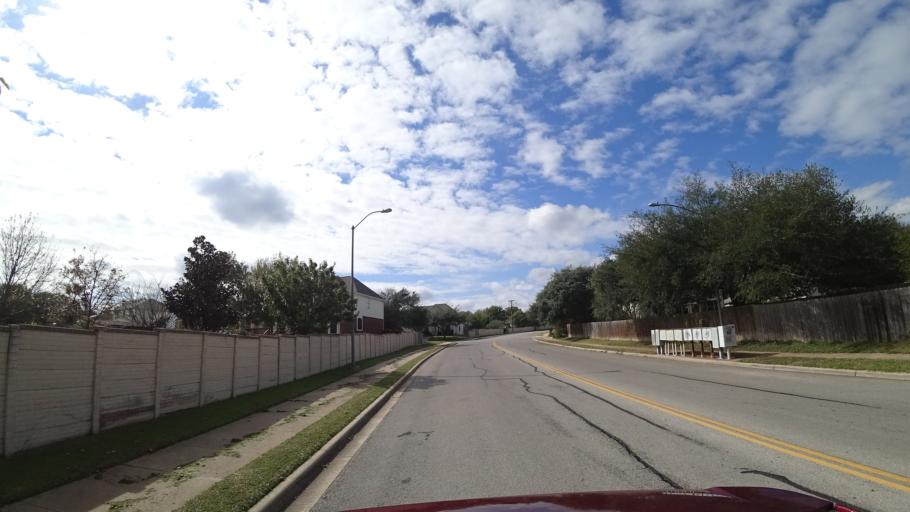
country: US
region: Texas
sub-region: Travis County
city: Pflugerville
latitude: 30.4407
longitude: -97.6375
